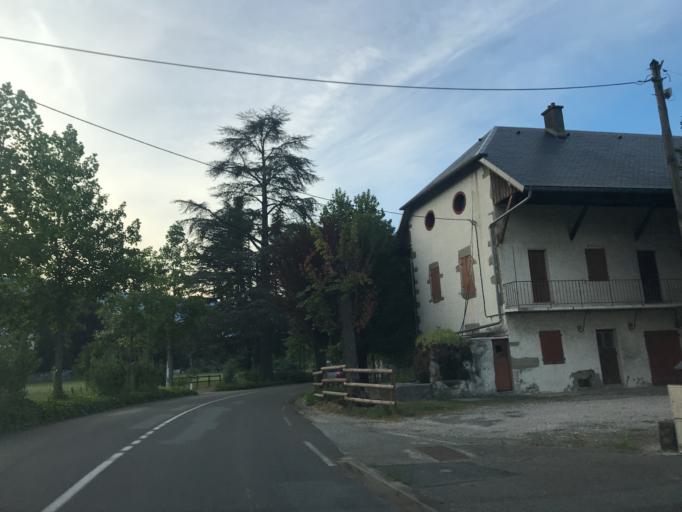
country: FR
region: Rhone-Alpes
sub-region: Departement de la Savoie
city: Cognin
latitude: 45.5750
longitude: 5.8884
